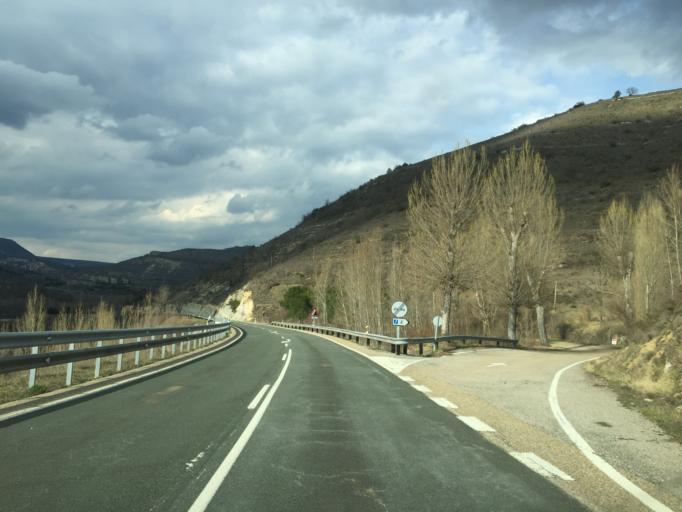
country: ES
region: Castille and Leon
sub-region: Provincia de Burgos
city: Tubilla del Agua
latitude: 42.7155
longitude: -3.8013
